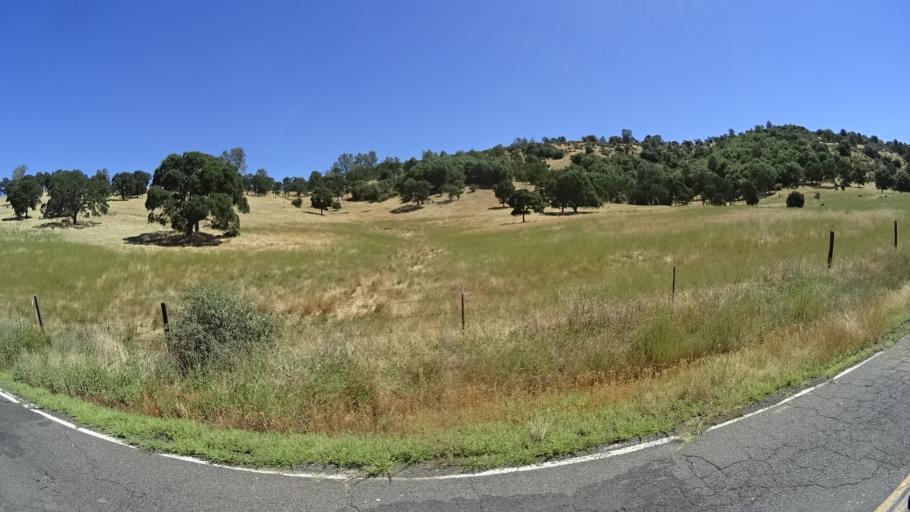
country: US
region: California
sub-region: Calaveras County
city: Copperopolis
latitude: 38.0058
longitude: -120.6659
